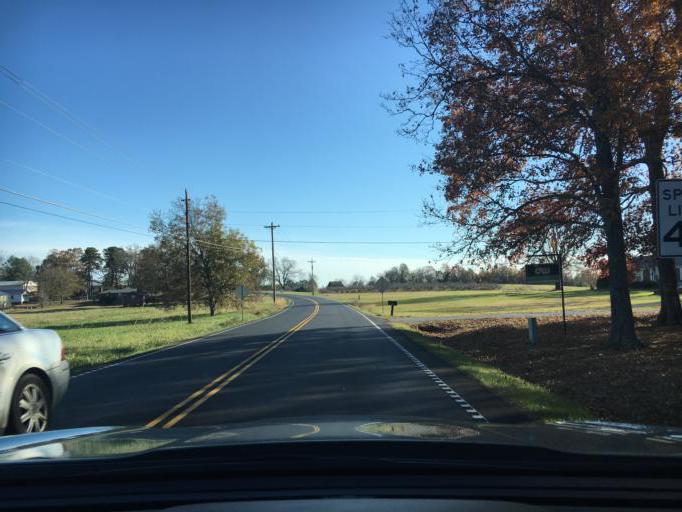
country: US
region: South Carolina
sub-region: Spartanburg County
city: Inman Mills
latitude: 35.0352
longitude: -82.1290
